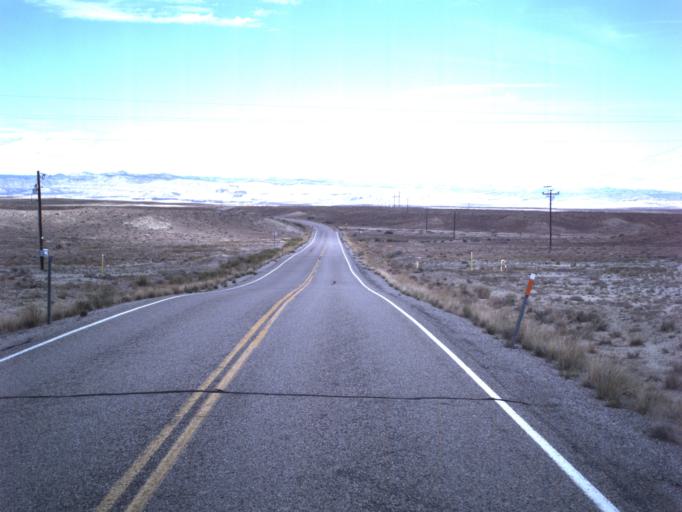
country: US
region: Utah
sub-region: Grand County
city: Moab
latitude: 38.9369
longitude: -109.3472
